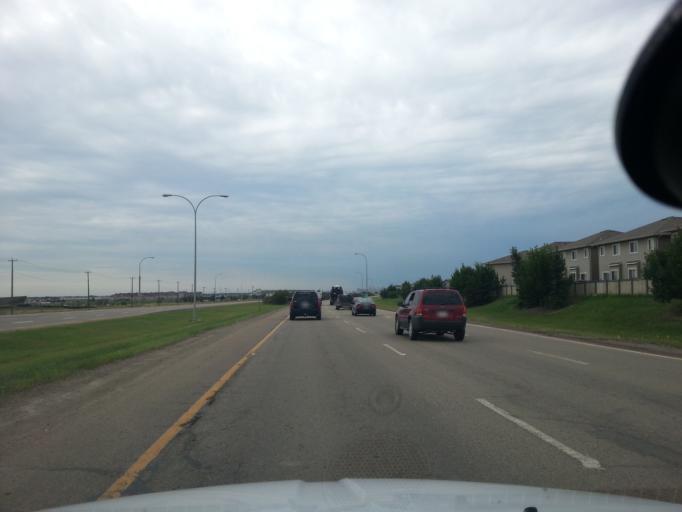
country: CA
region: Alberta
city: Edmonton
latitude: 53.6140
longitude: -113.4040
